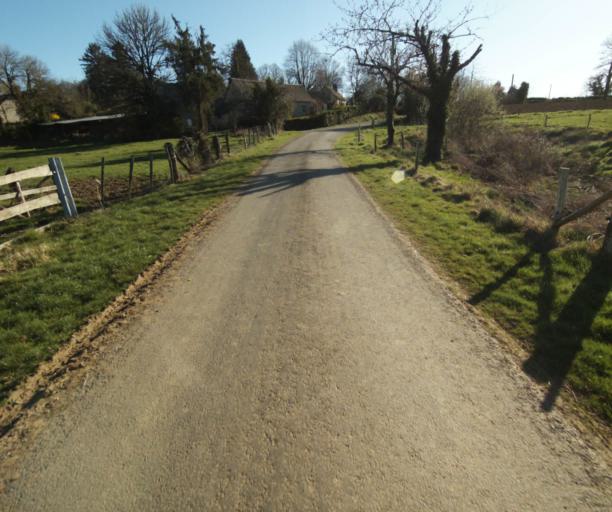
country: FR
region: Limousin
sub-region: Departement de la Correze
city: Seilhac
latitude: 45.3828
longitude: 1.6881
